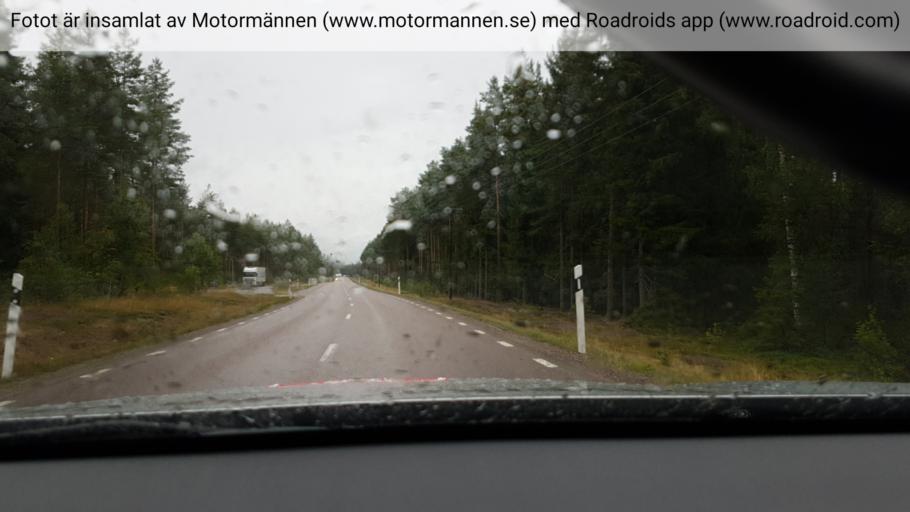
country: SE
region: Gaevleborg
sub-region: Gavle Kommun
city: Hedesunda
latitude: 60.5239
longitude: 16.9468
